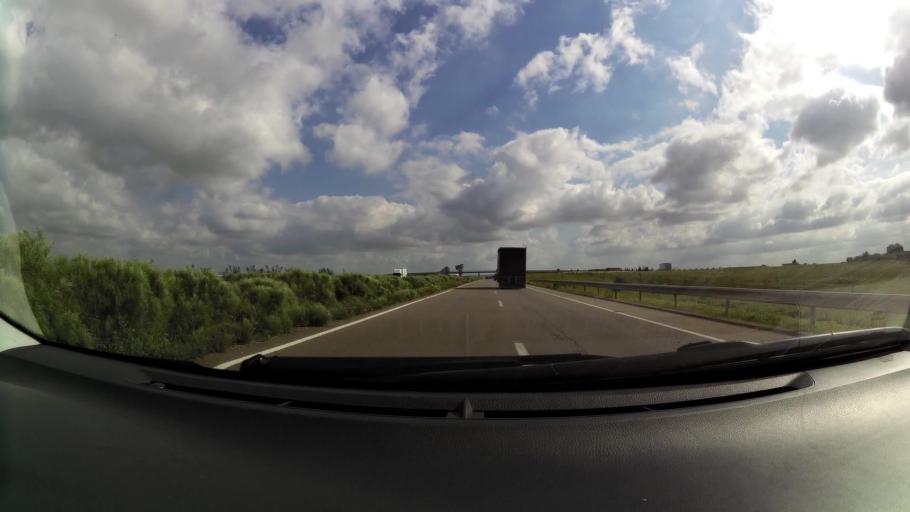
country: MA
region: Chaouia-Ouardigha
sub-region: Settat Province
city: Berrechid
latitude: 33.2077
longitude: -7.5754
